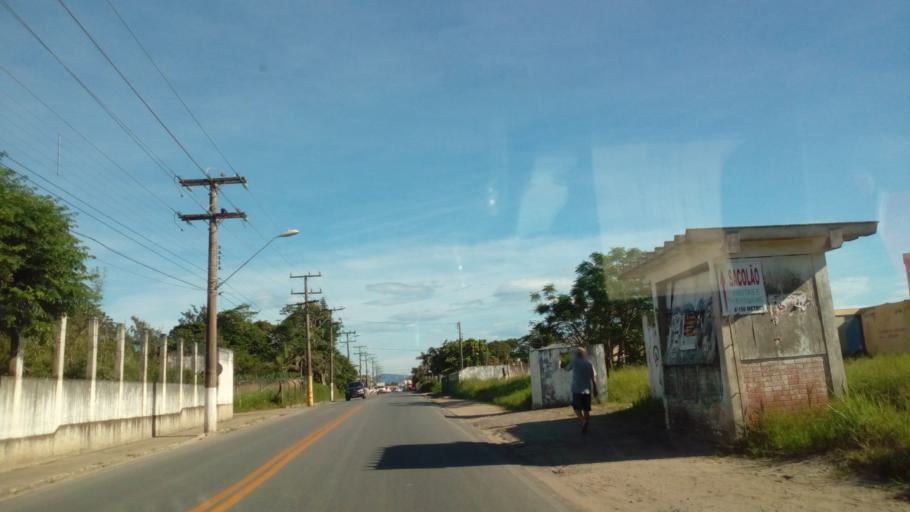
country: BR
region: Santa Catarina
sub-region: Laguna
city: Laguna
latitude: -28.4671
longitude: -48.7853
